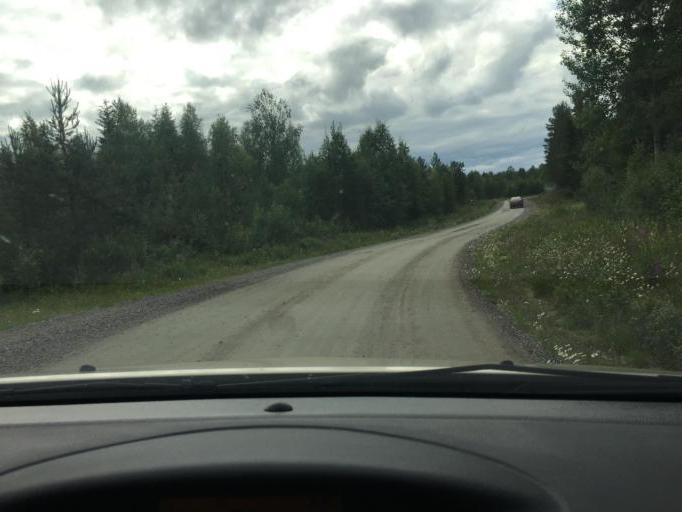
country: SE
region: Norrbotten
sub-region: Overkalix Kommun
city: OEverkalix
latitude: 66.0916
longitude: 22.8214
